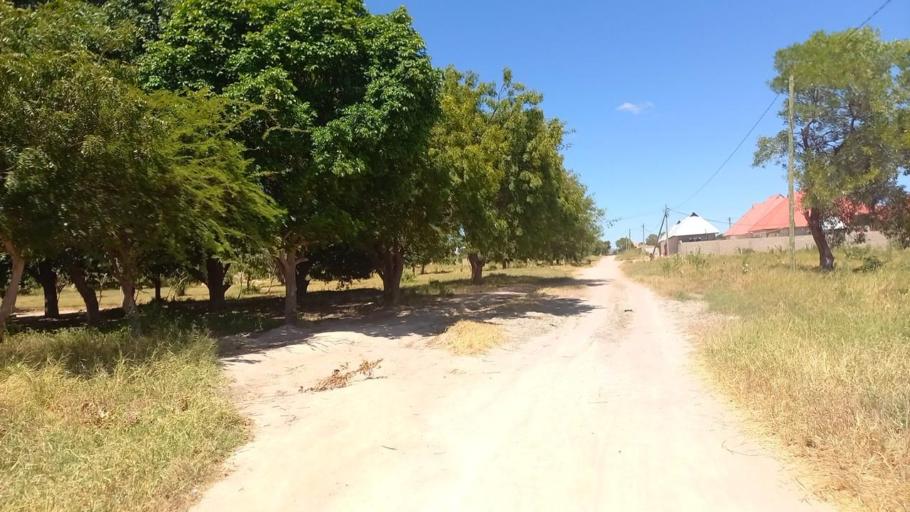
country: TZ
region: Dodoma
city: Dodoma
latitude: -6.1166
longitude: 35.7394
